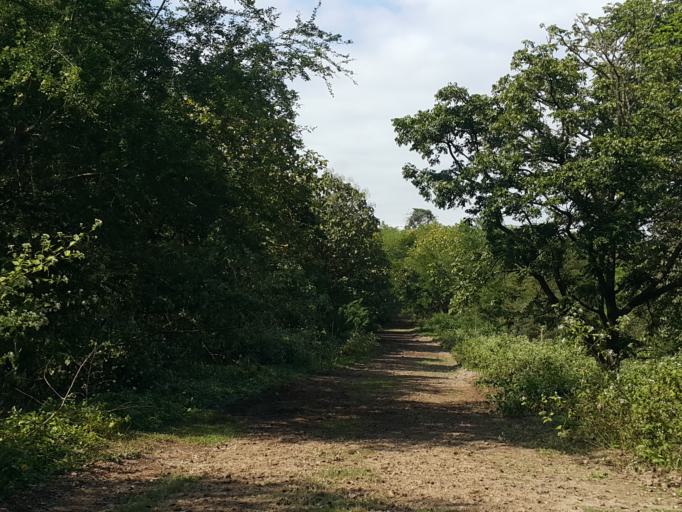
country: TH
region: Lampang
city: Mae Mo
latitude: 18.3424
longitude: 99.7702
